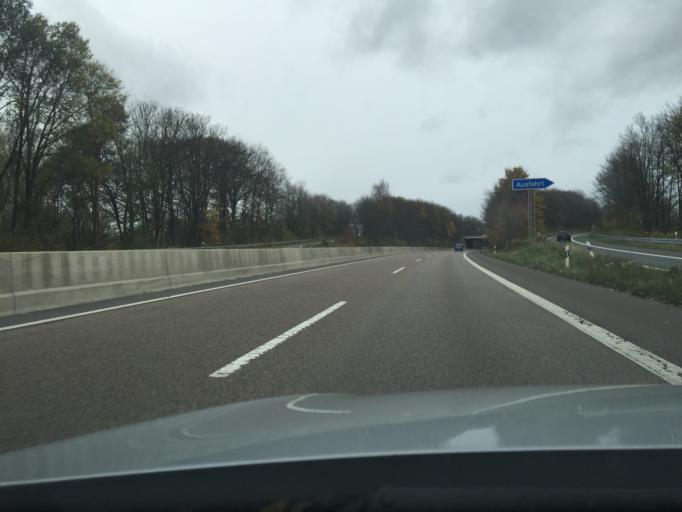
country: DE
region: North Rhine-Westphalia
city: Wulfrath
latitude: 51.2970
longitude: 7.0671
